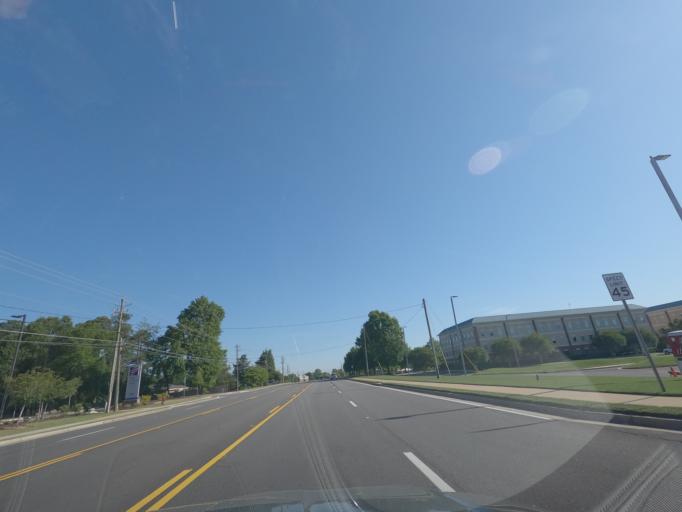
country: US
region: Georgia
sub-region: Columbia County
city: Evans
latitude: 33.5312
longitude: -82.1307
